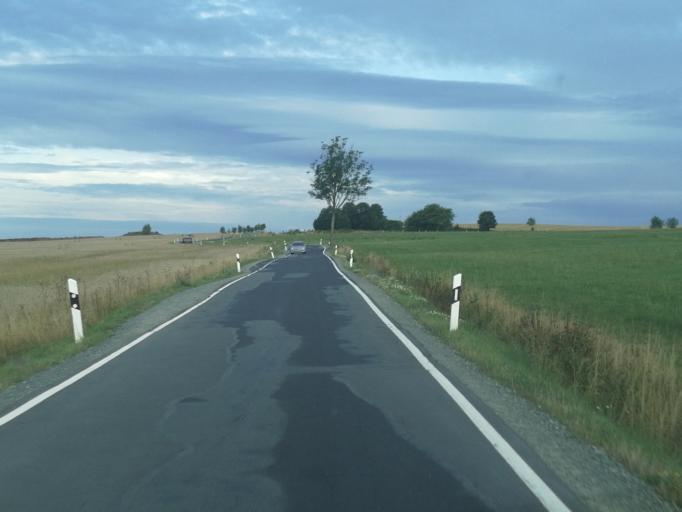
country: DE
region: Saxony
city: Triebel
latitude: 50.3343
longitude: 12.0959
